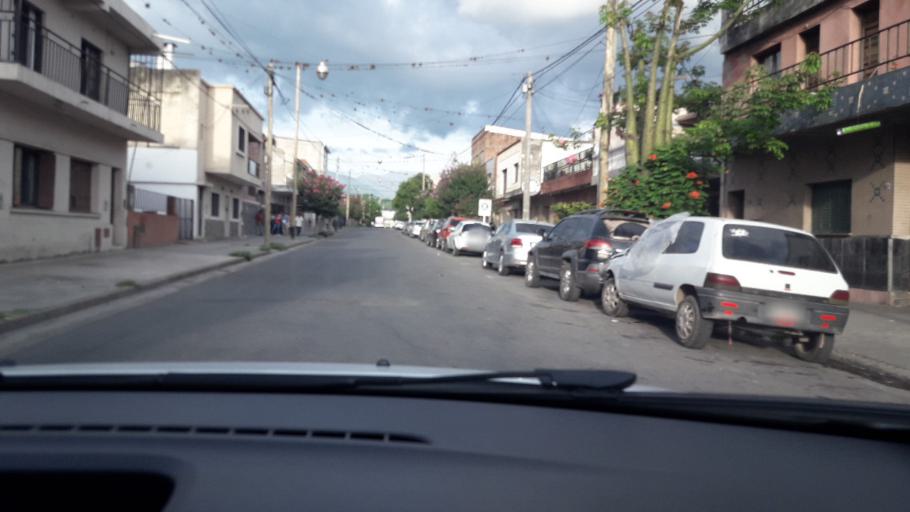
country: AR
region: Jujuy
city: San Salvador de Jujuy
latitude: -24.1915
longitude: -65.3053
